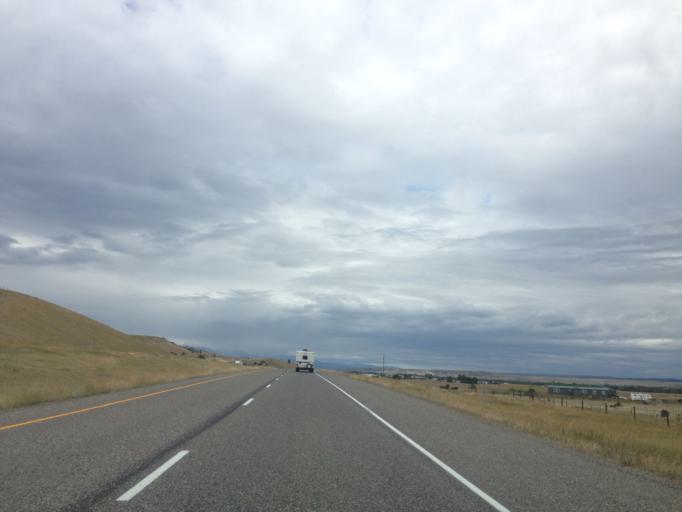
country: US
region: Montana
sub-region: Sweet Grass County
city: Big Timber
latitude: 45.7428
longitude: -109.7673
